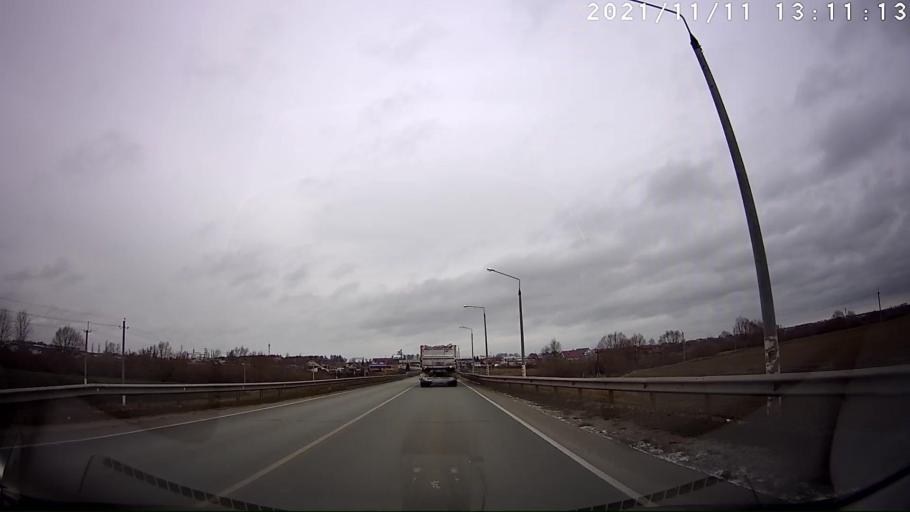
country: RU
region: Chuvashia
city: Batyrevo
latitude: 55.0702
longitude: 47.5796
